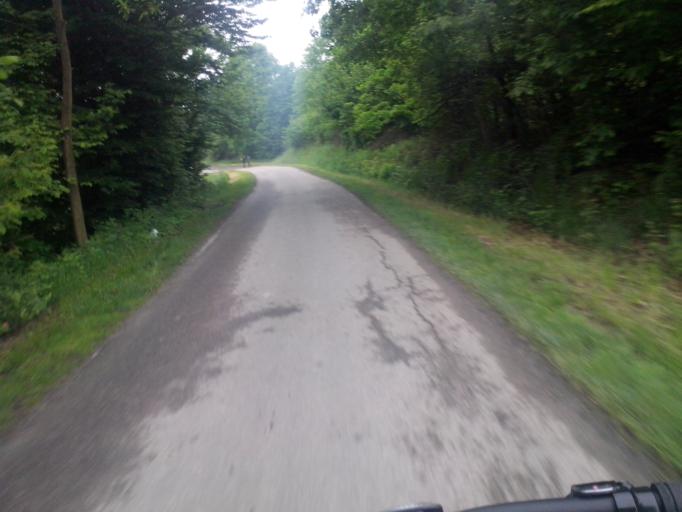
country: PL
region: Subcarpathian Voivodeship
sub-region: Powiat strzyzowski
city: Strzyzow
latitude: 49.8688
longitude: 21.8094
